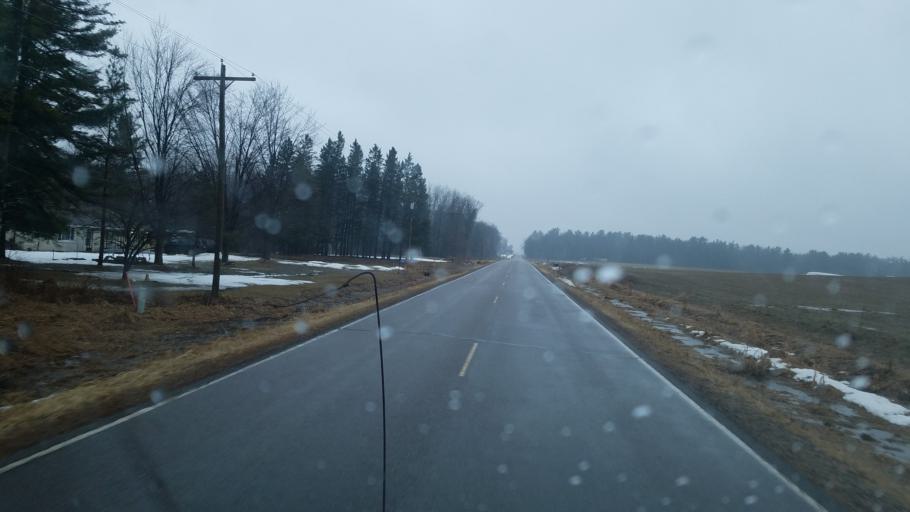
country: US
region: Wisconsin
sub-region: Wood County
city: Marshfield
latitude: 44.4734
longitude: -90.2800
